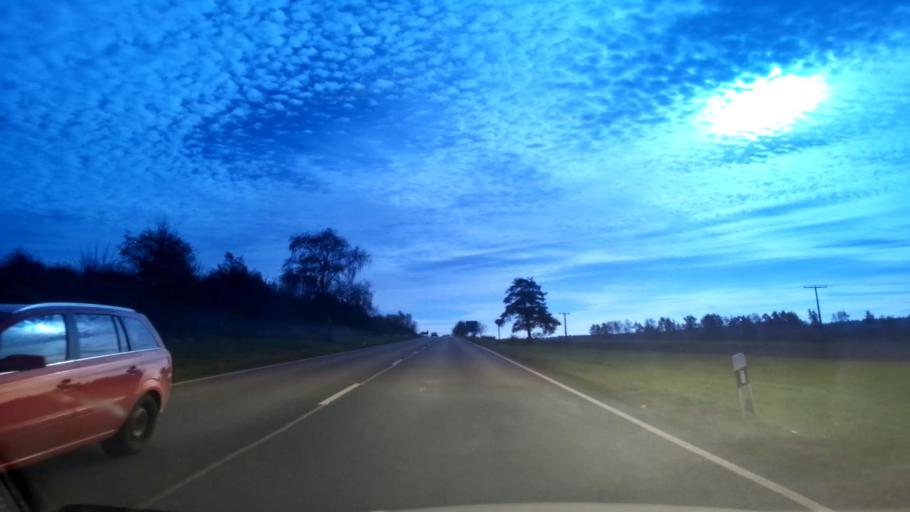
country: DE
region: Bavaria
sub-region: Upper Palatinate
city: Pechbrunn
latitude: 49.9819
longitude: 12.1311
